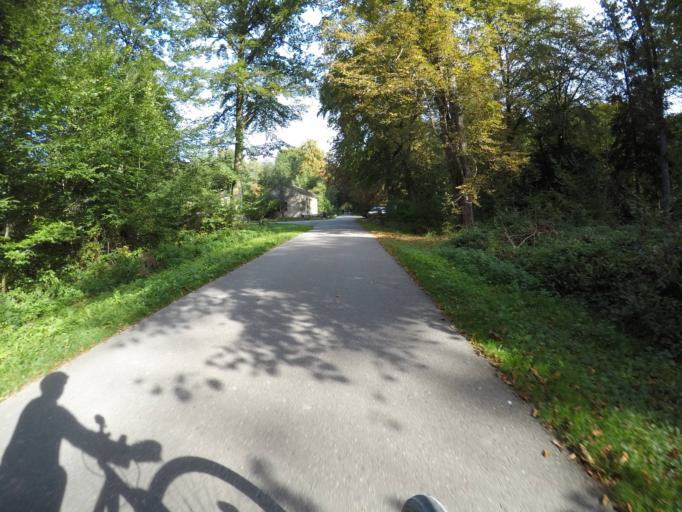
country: DE
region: Baden-Wuerttemberg
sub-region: Regierungsbezirk Stuttgart
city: Gerlingen
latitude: 48.7660
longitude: 9.0911
